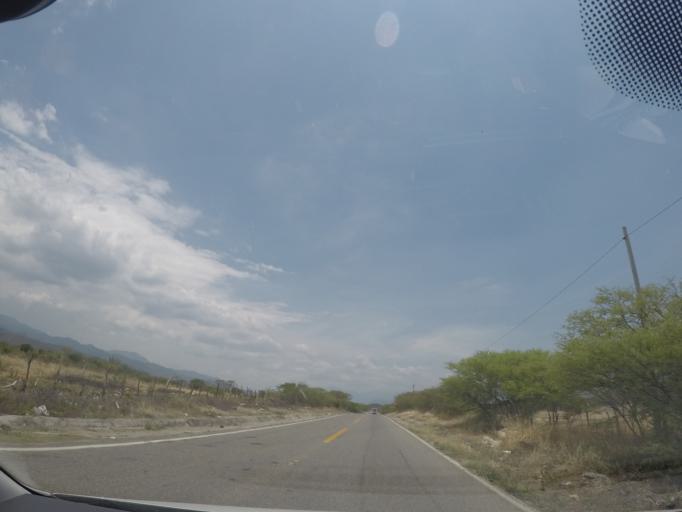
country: MX
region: Oaxaca
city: Magdalena Tequisistlan
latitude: 16.4075
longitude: -95.5795
